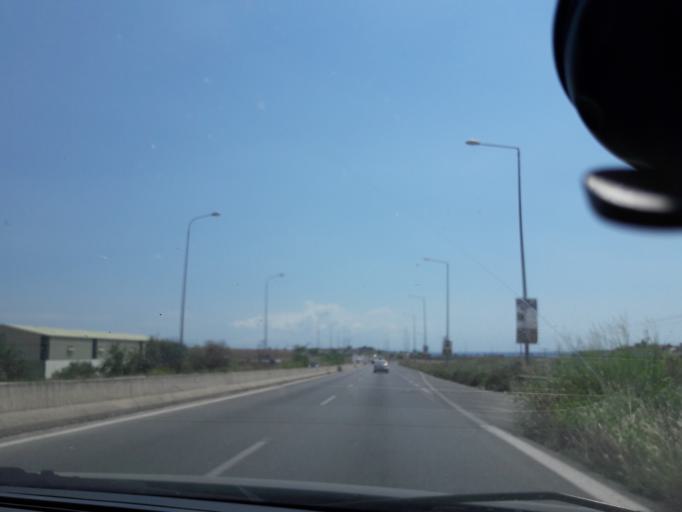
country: GR
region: Central Macedonia
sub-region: Nomos Chalkidikis
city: Nea Triglia
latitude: 40.2904
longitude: 23.1449
